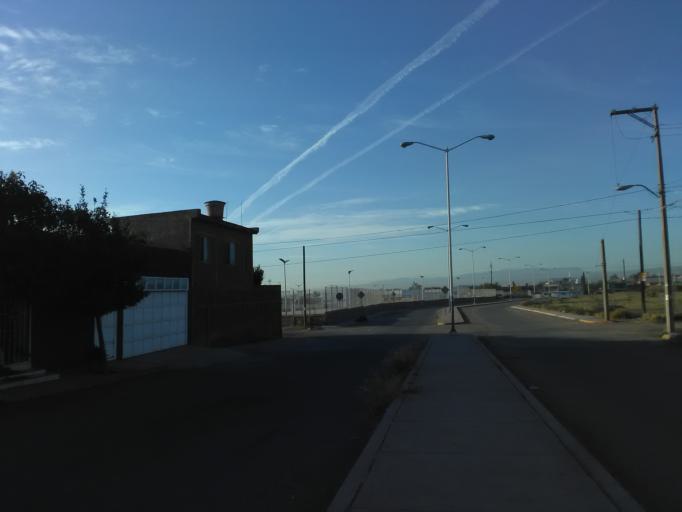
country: MX
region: Durango
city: Victoria de Durango
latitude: 24.0486
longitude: -104.6620
